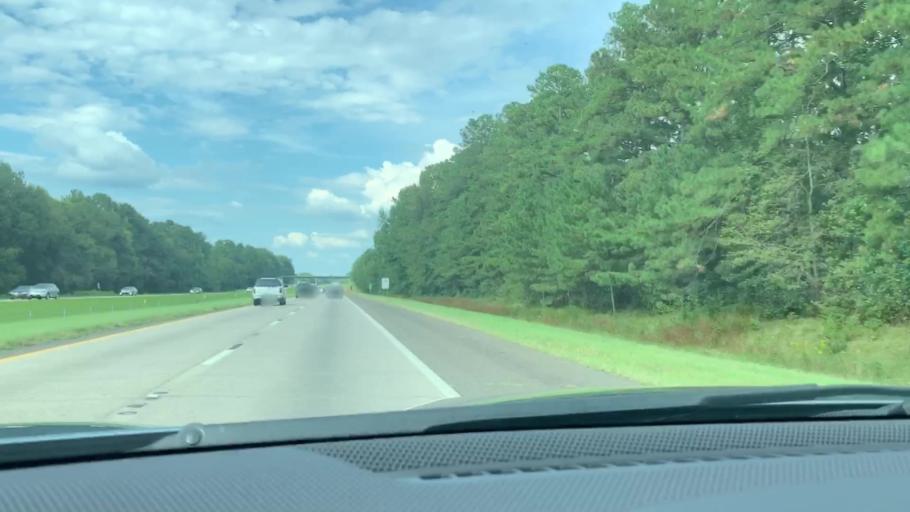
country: US
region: South Carolina
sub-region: Hampton County
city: Yemassee
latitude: 32.6727
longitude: -80.8830
